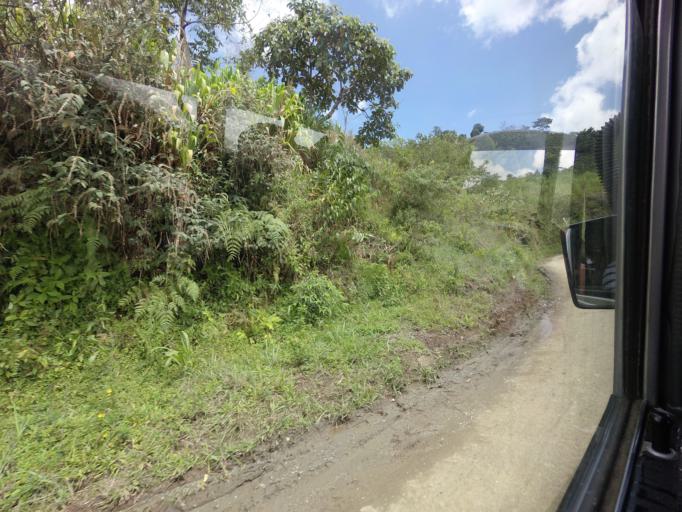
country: CO
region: Huila
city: Isnos
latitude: 1.9481
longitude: -76.2777
